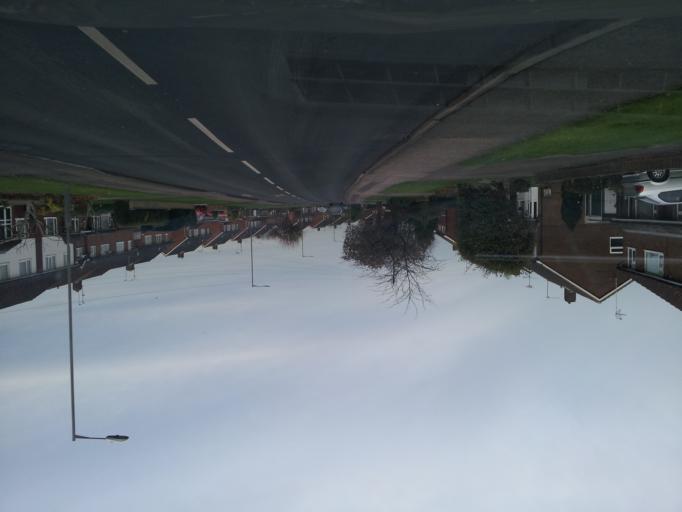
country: GB
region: England
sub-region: Buckinghamshire
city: Weston Turville
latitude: 51.8081
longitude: -0.7787
